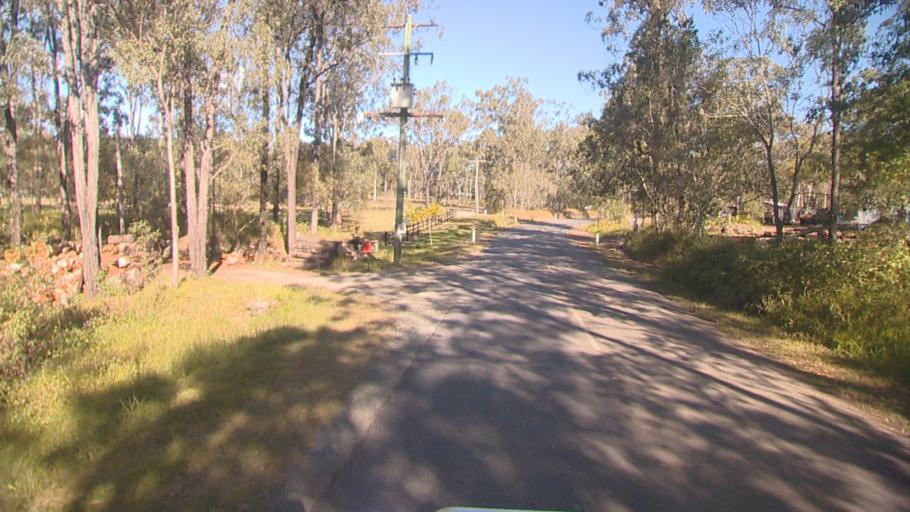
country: AU
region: Queensland
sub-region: Logan
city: Chambers Flat
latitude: -27.8153
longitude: 153.0710
